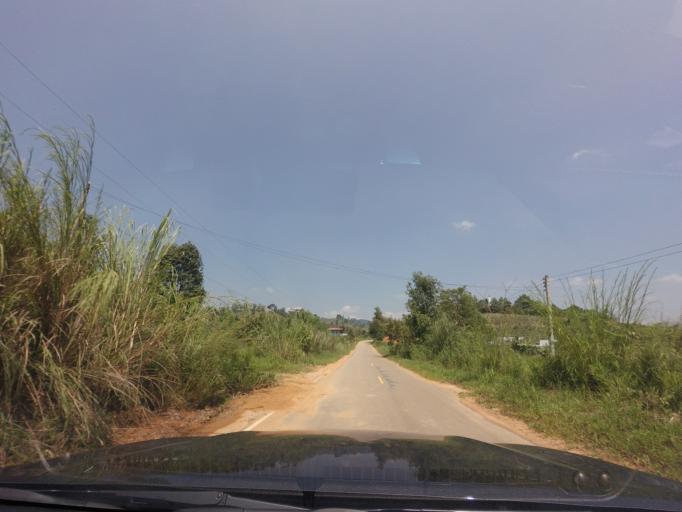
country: TH
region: Loei
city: Na Haeo
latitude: 17.5465
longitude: 100.8787
